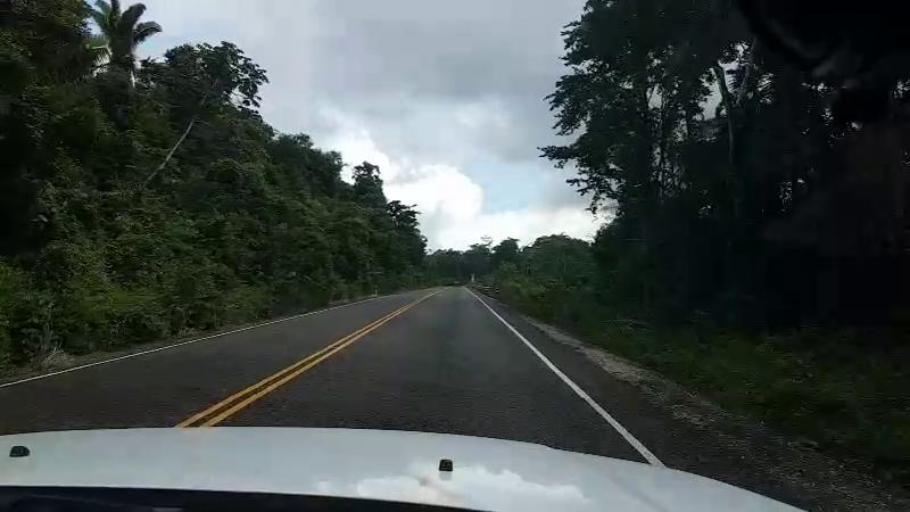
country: BZ
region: Cayo
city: Belmopan
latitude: 17.1549
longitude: -88.6798
